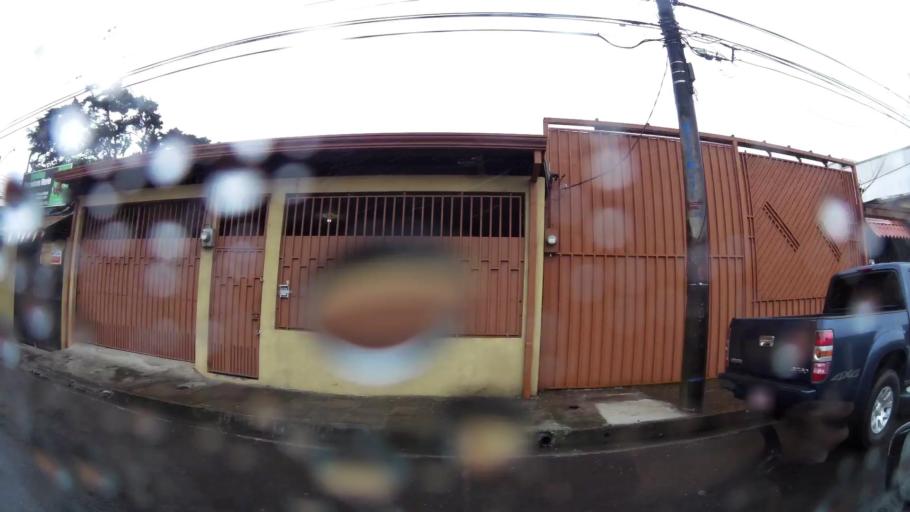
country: CR
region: Cartago
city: Cartago
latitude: 9.8644
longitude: -83.9305
